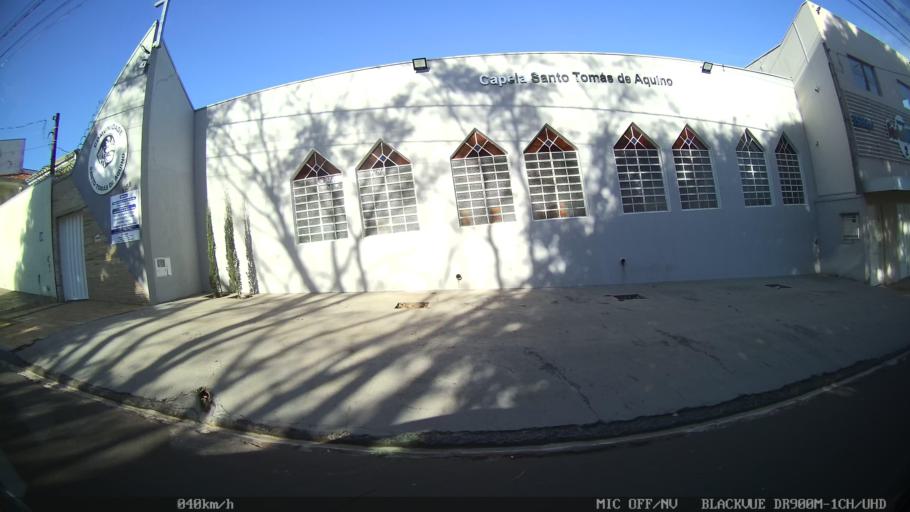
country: BR
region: Sao Paulo
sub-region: Franca
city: Franca
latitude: -20.5075
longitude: -47.4108
